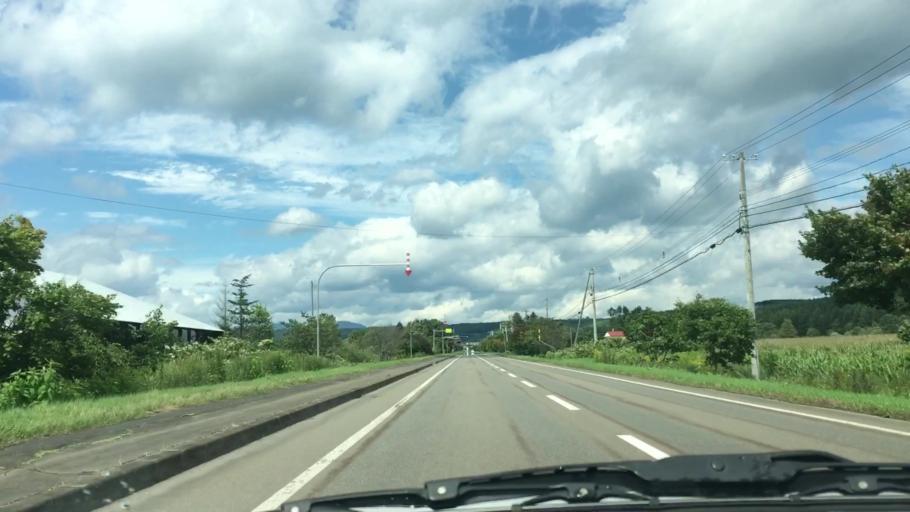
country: JP
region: Hokkaido
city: Otofuke
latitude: 43.2918
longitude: 143.3084
